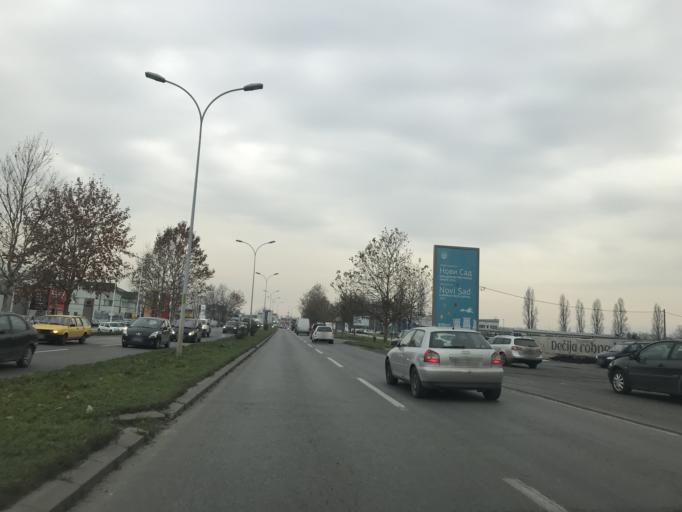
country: RS
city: Veternik
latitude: 45.2458
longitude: 19.7719
